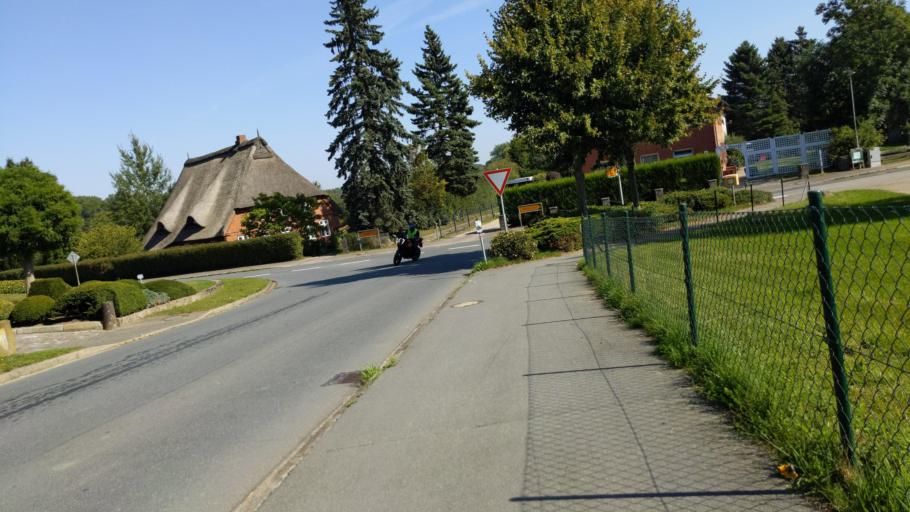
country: DE
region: Schleswig-Holstein
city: Meddewade
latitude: 53.8165
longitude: 10.4569
